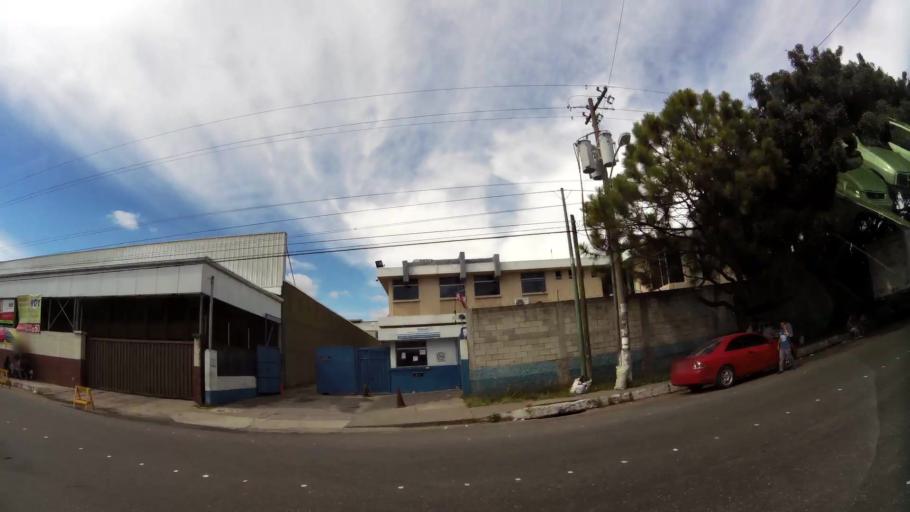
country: GT
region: Guatemala
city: Mixco
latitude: 14.6392
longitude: -90.5825
